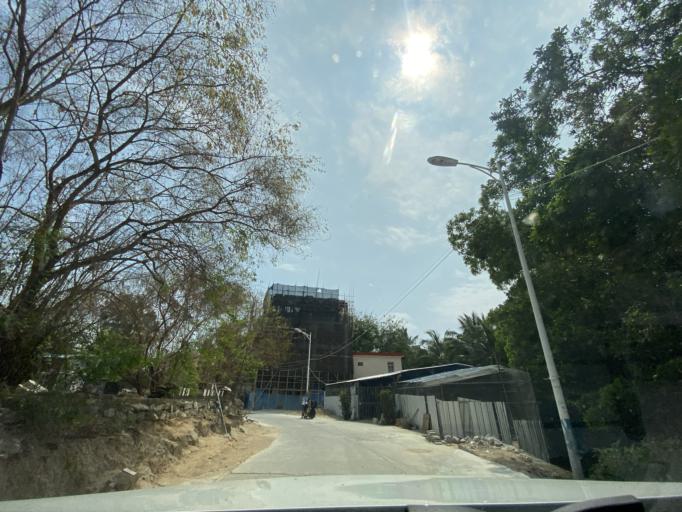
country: CN
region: Hainan
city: Yingzhou
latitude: 18.4263
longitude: 109.8533
